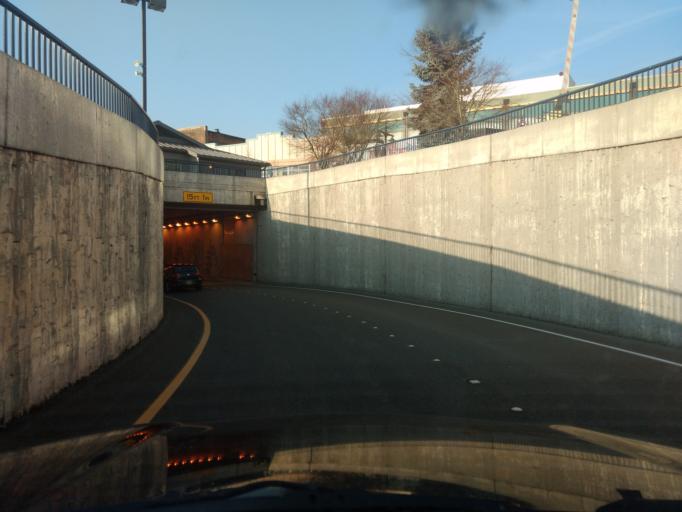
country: US
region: Washington
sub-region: Kitsap County
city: Bremerton
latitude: 47.5632
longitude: -122.6255
